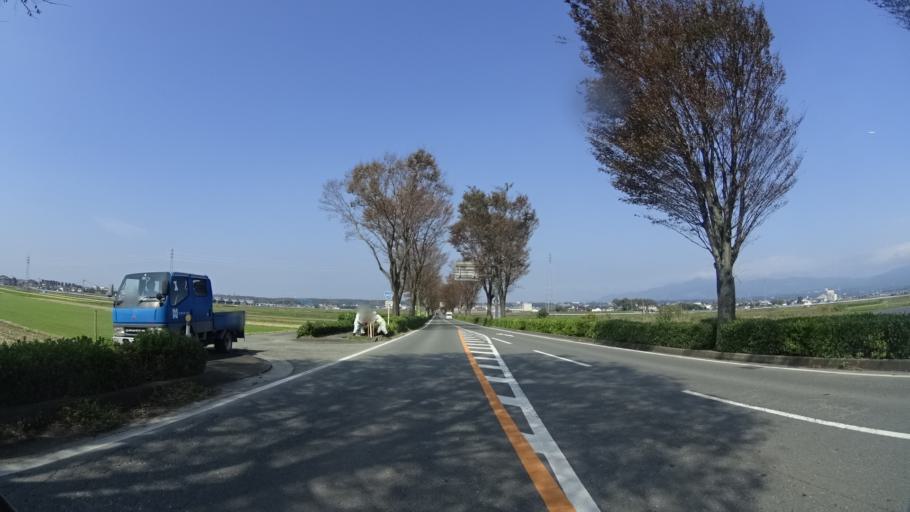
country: JP
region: Kumamoto
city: Ozu
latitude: 32.8581
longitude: 130.8552
